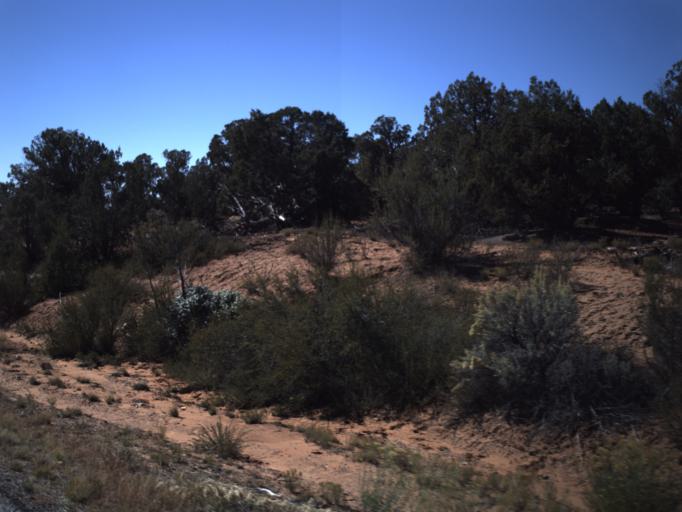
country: US
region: Utah
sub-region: San Juan County
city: Blanding
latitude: 37.4460
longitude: -109.9205
